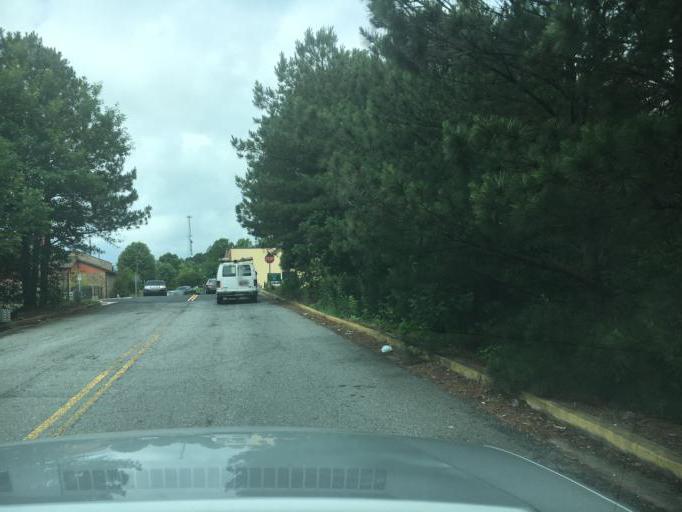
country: US
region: Georgia
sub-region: Gwinnett County
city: Dacula
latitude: 34.0722
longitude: -83.9145
